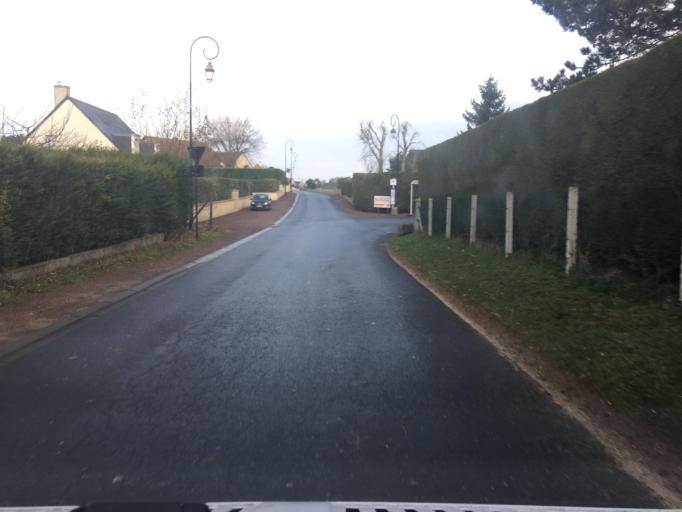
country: FR
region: Lower Normandy
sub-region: Departement du Calvados
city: Rots
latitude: 49.2020
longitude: -0.4637
